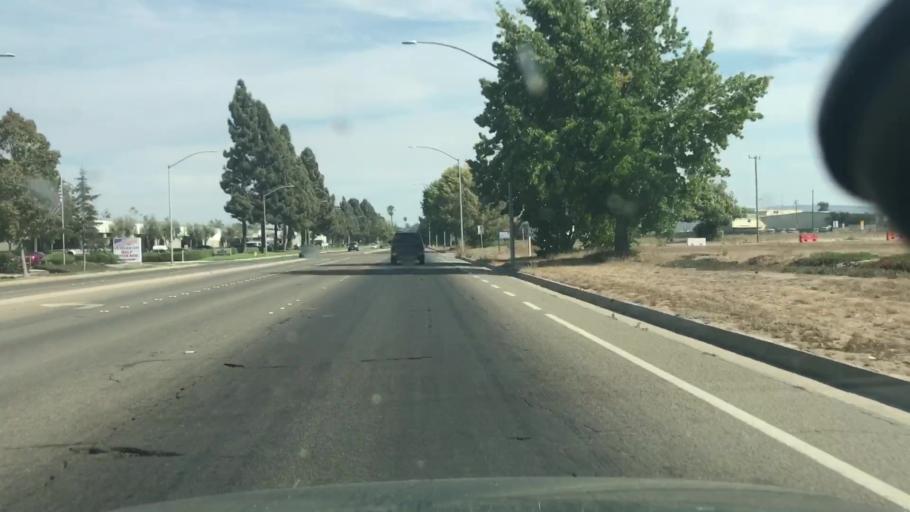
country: US
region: California
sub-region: Santa Barbara County
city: Orcutt
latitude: 34.9052
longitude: -120.4523
